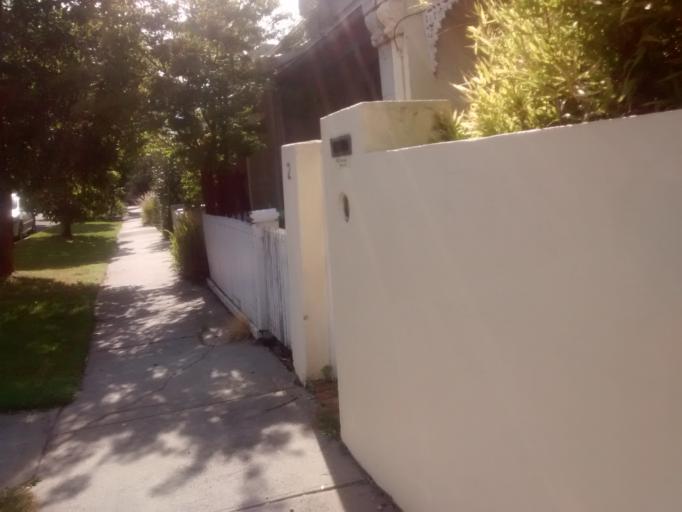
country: AU
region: Victoria
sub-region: Darebin
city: Northcote
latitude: -37.7802
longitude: 144.9927
